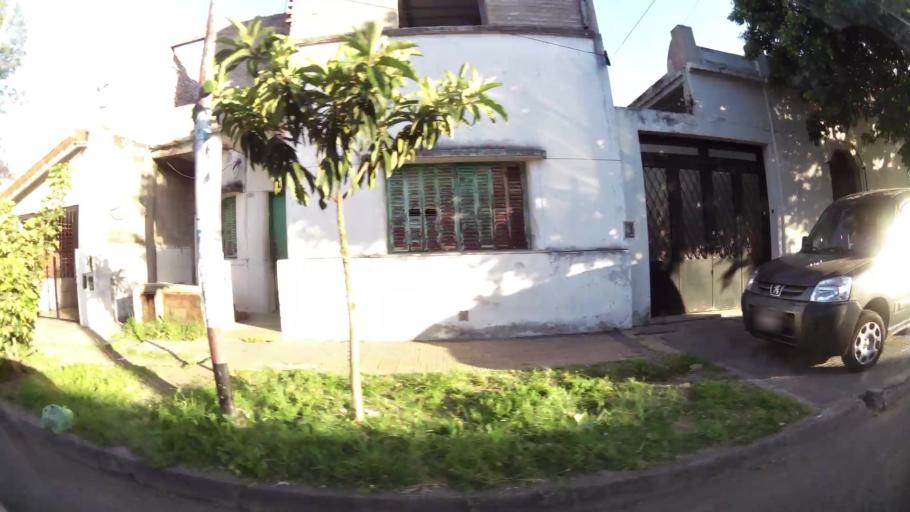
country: AR
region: Buenos Aires
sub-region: Partido de General San Martin
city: General San Martin
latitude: -34.5713
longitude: -58.5484
